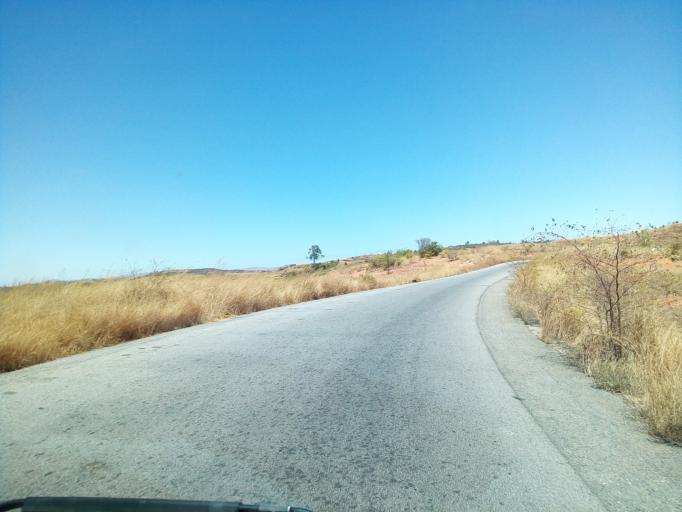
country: MG
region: Betsiboka
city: Maevatanana
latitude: -16.9378
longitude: 46.9461
